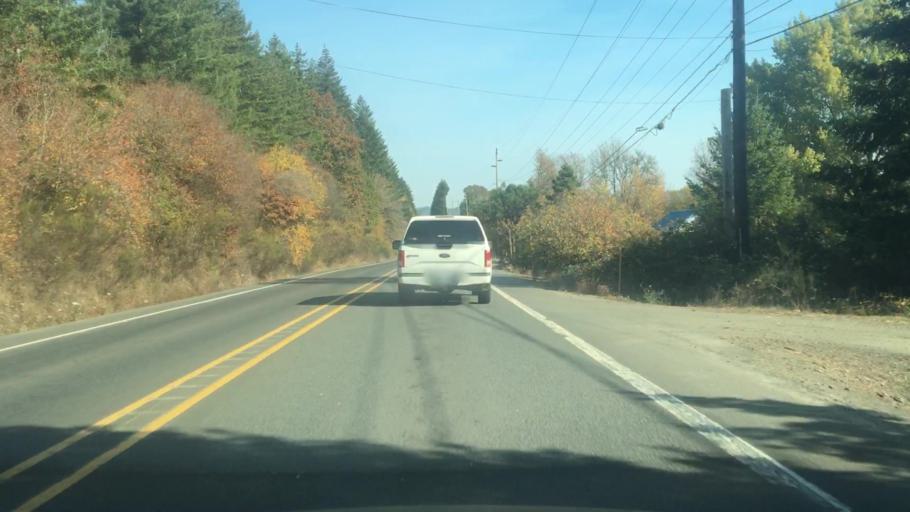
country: US
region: Oregon
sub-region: Polk County
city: Grand Ronde
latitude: 45.0585
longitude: -123.5987
